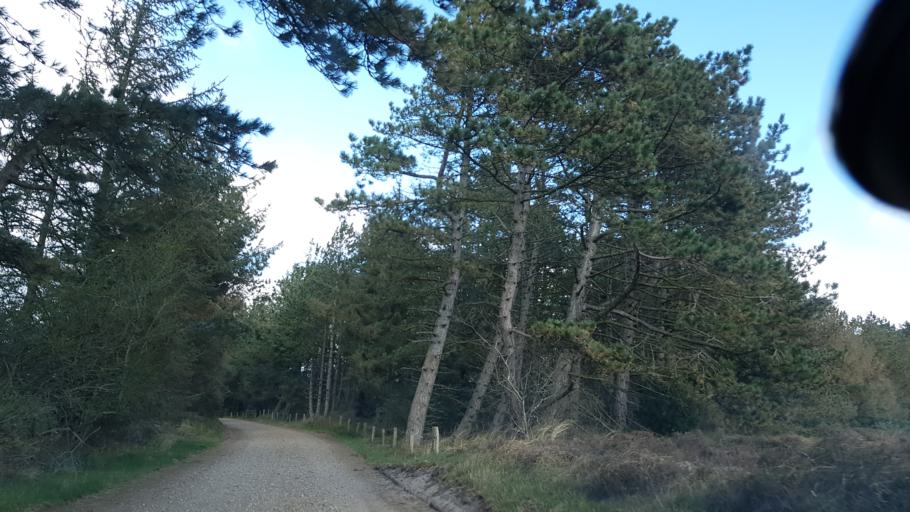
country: DE
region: Schleswig-Holstein
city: List
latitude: 55.1028
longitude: 8.5356
